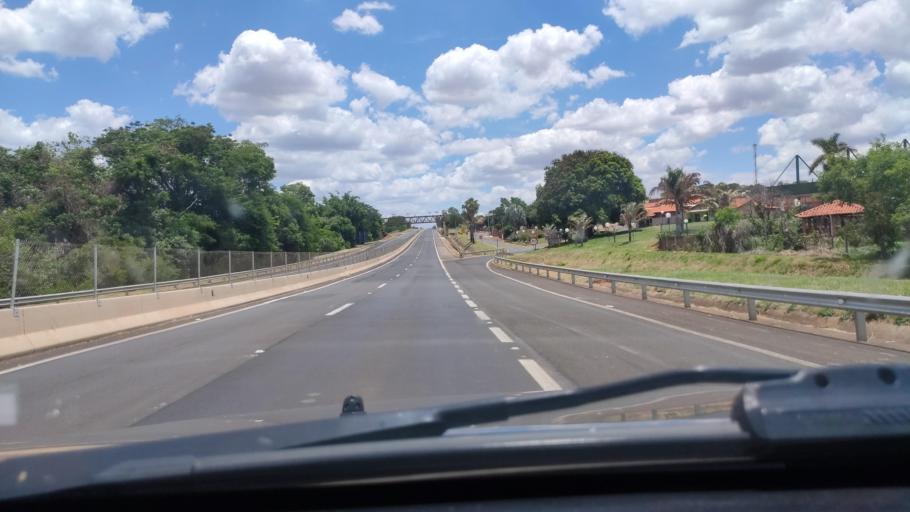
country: BR
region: Sao Paulo
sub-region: Duartina
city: Duartina
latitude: -22.6962
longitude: -49.4278
